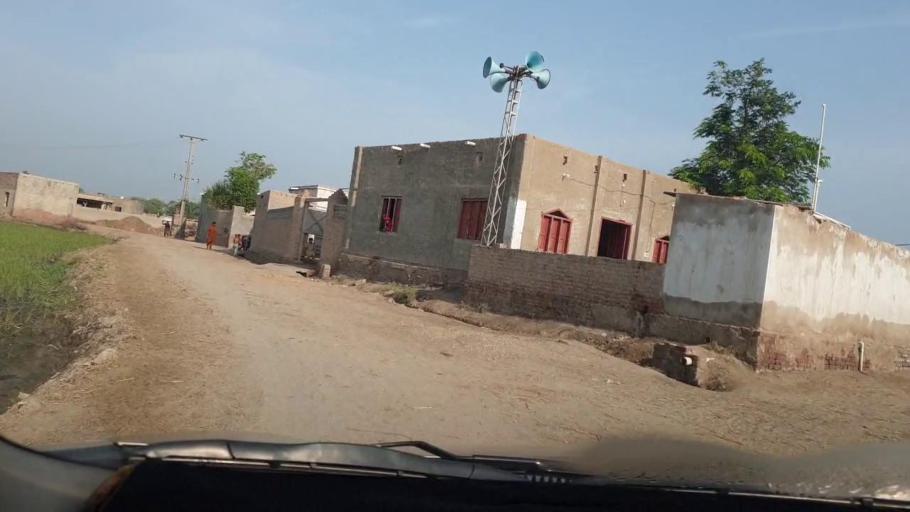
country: PK
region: Sindh
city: Goth Garelo
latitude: 27.4873
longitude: 68.0673
